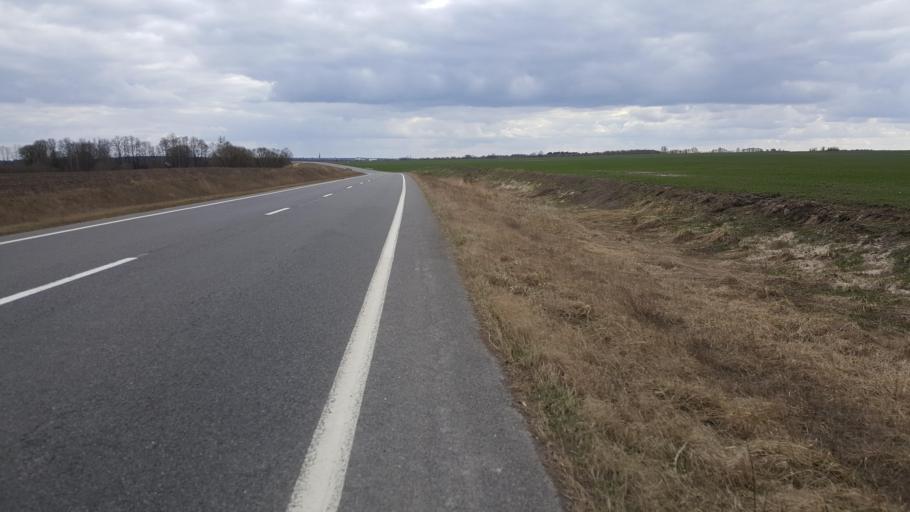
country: BY
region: Brest
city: Kamyanyets
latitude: 52.4418
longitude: 23.8318
